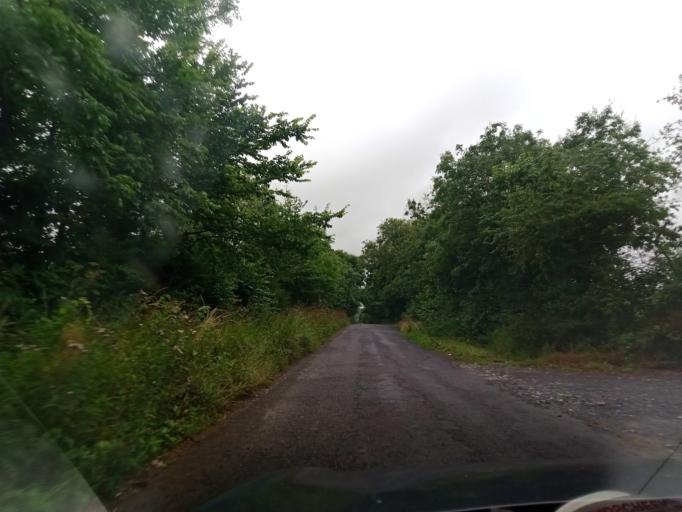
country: IE
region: Leinster
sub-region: Laois
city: Abbeyleix
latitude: 52.9202
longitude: -7.2854
